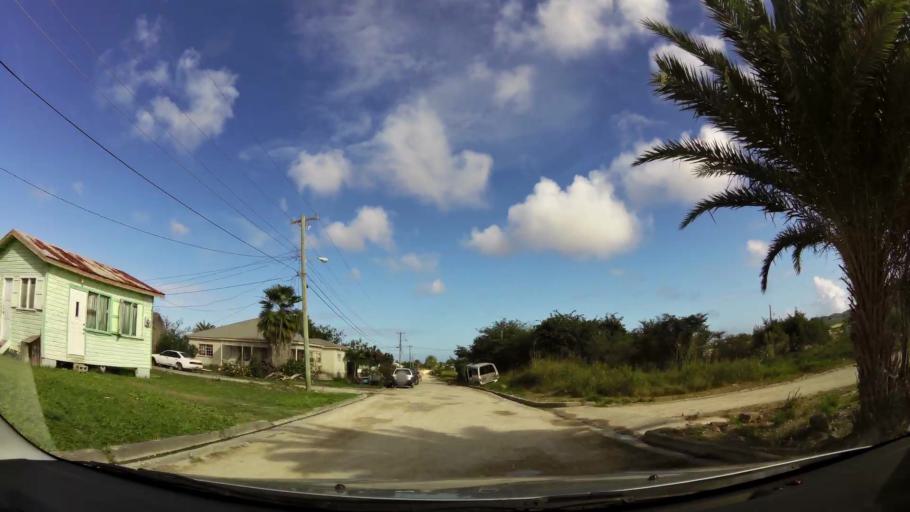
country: AG
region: Saint Peter
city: All Saints
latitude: 17.0670
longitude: -61.7867
